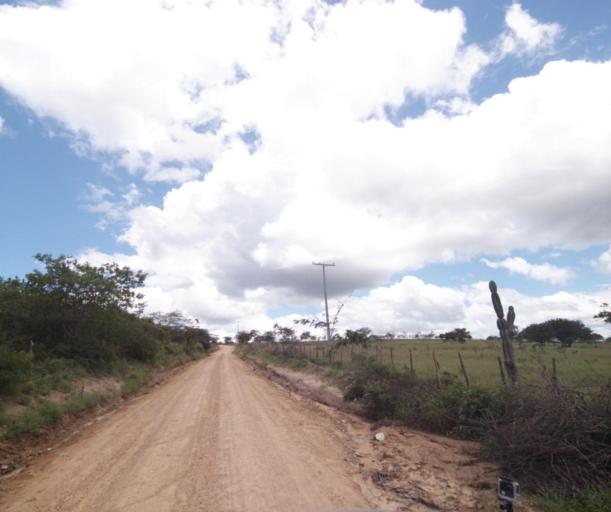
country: BR
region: Bahia
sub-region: Pocoes
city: Pocoes
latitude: -14.3820
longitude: -40.3723
